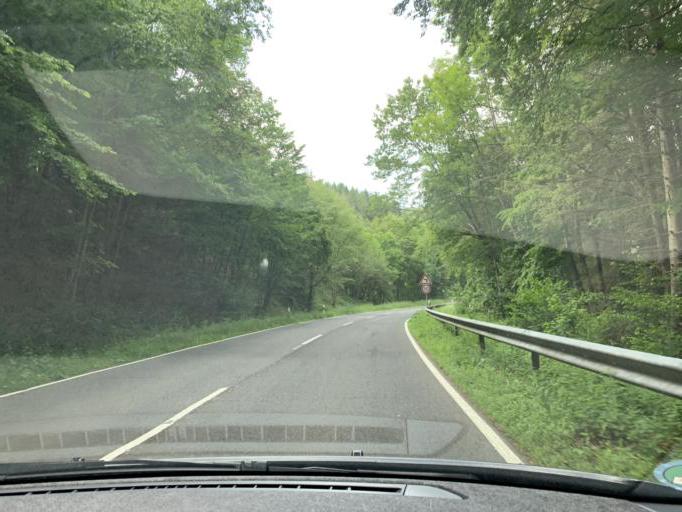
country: DE
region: North Rhine-Westphalia
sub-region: Regierungsbezirk Koln
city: Hurtgenwald
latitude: 50.6865
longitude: 6.4072
